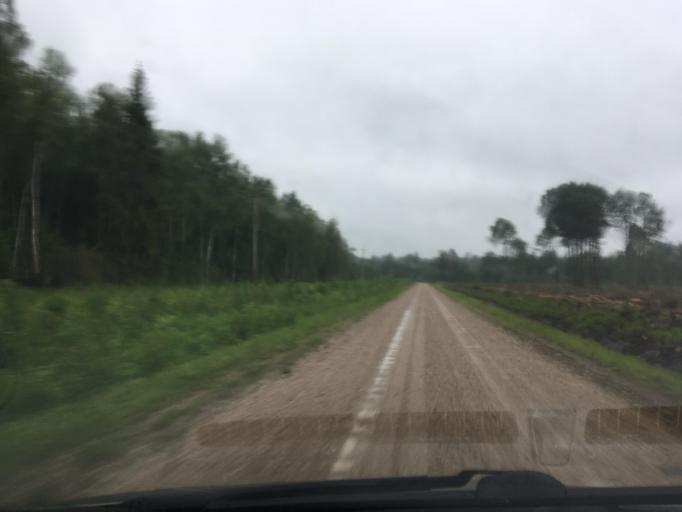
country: EE
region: Laeaene
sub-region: Lihula vald
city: Lihula
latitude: 58.6122
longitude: 23.8269
